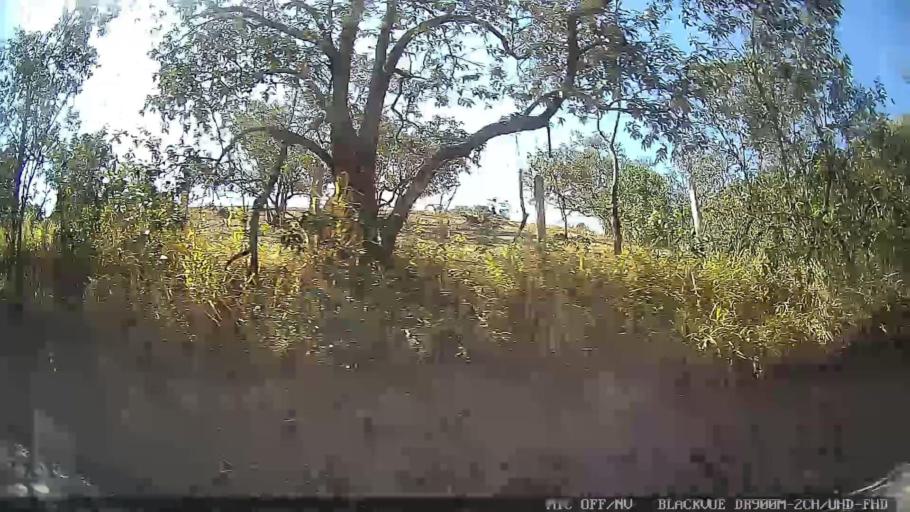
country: BR
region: Sao Paulo
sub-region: Jacarei
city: Jacarei
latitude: -23.3416
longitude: -46.0035
